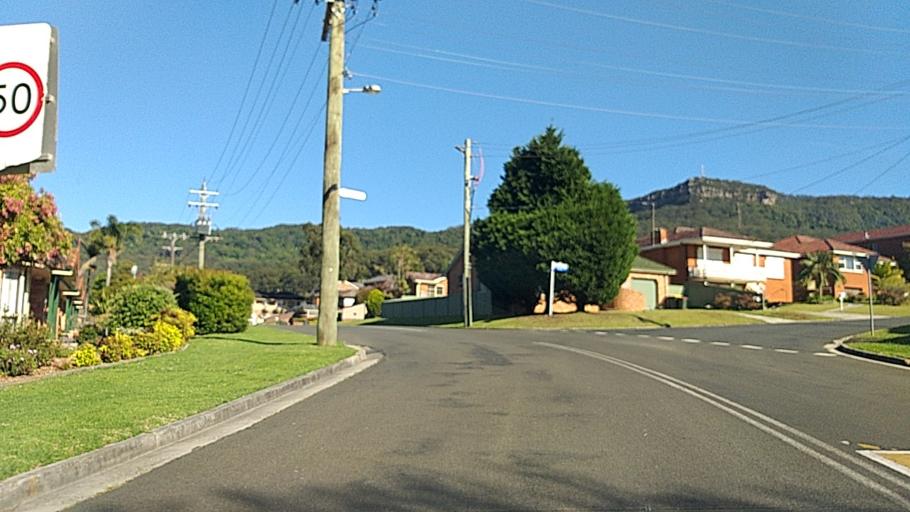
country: AU
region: New South Wales
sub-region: Wollongong
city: Corrimal
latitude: -34.3800
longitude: 150.8874
